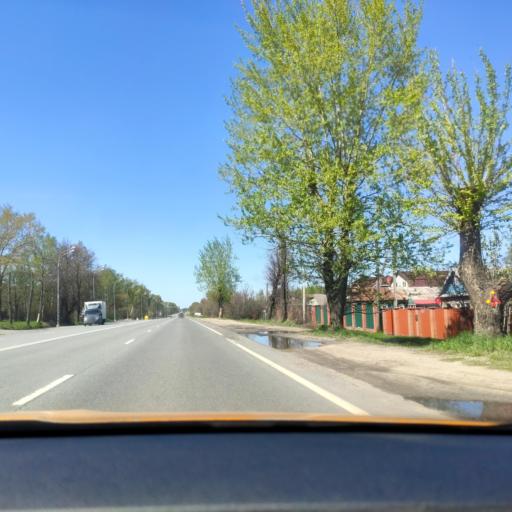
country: RU
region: Moskovskaya
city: Beloozerskiy
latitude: 55.3726
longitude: 38.3845
